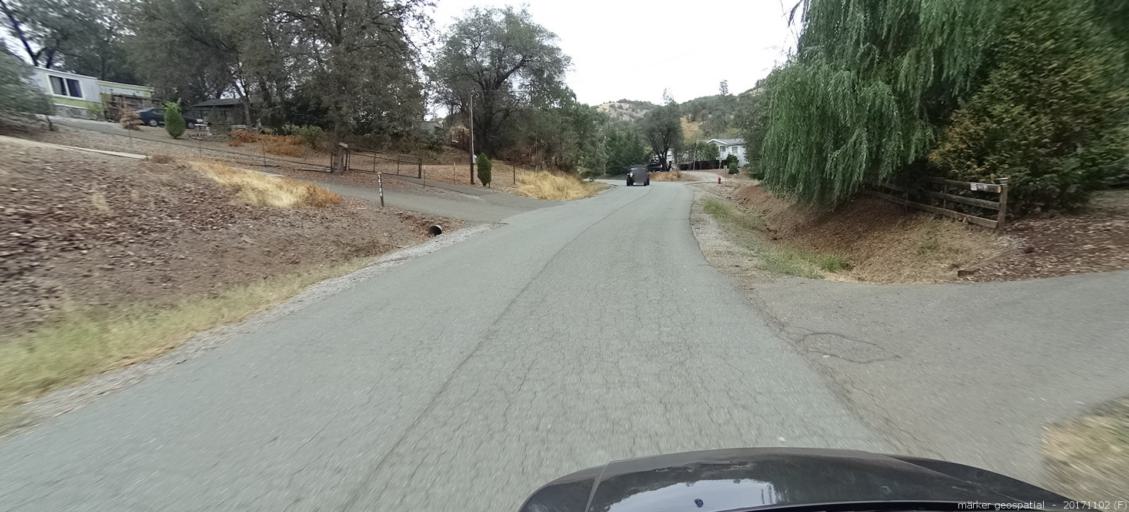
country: US
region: California
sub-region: Shasta County
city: Bella Vista
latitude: 40.7162
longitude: -122.2352
